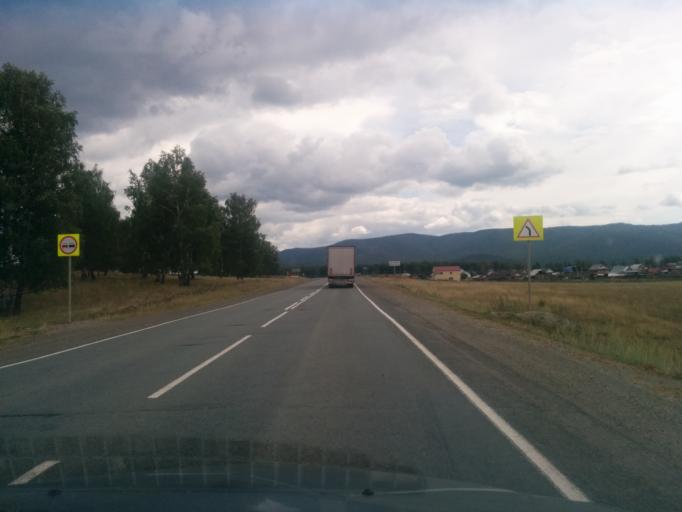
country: RU
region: Bashkortostan
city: Lomovka
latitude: 53.8858
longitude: 58.0987
